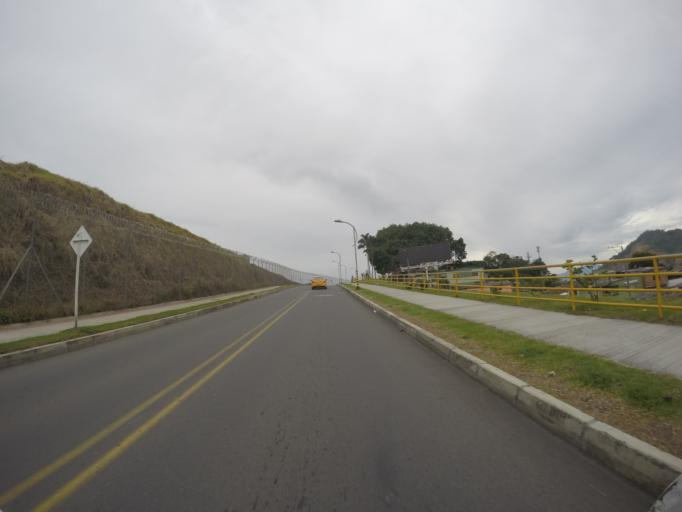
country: CO
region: Risaralda
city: Pereira
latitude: 4.8159
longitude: -75.7323
